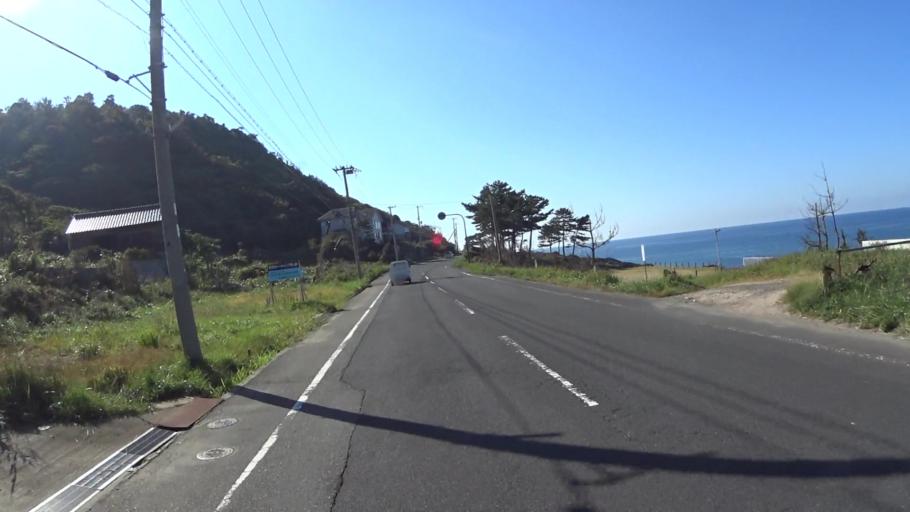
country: JP
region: Kyoto
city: Miyazu
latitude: 35.7177
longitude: 135.0743
